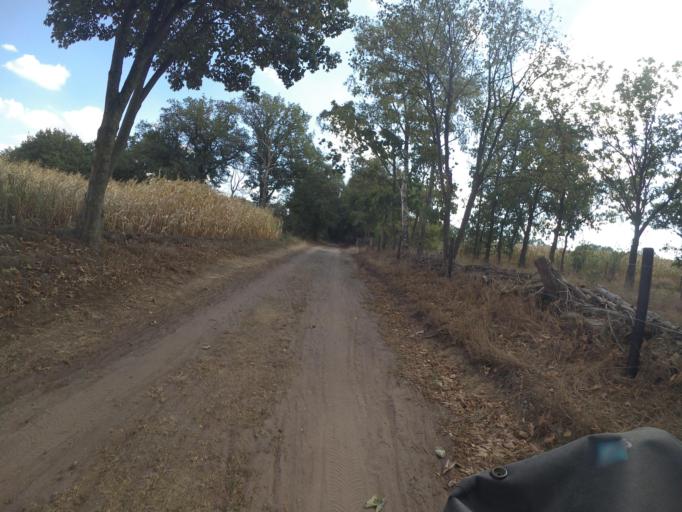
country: NL
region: Overijssel
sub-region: Gemeente Hof van Twente
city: Markelo
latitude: 52.2780
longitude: 6.4728
